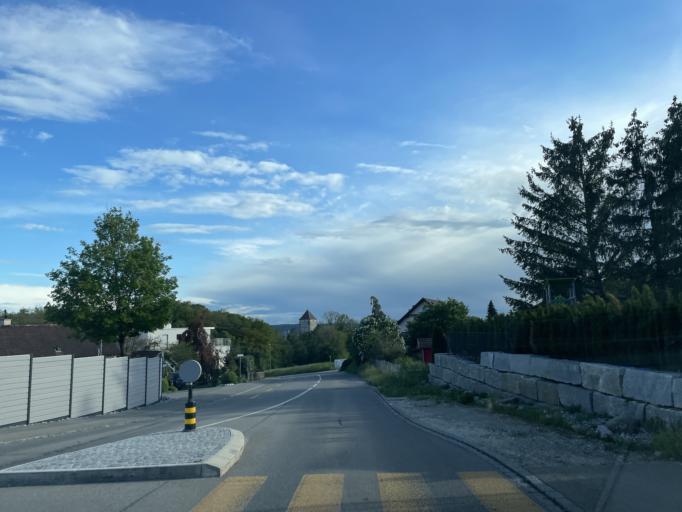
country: CH
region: Schaffhausen
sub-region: Bezirk Reiat
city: Stetten
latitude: 47.7374
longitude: 8.6622
